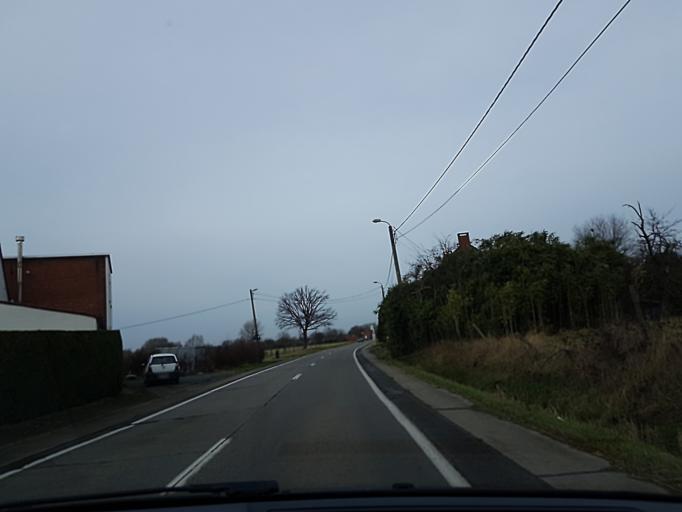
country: BE
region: Flanders
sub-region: Provincie Antwerpen
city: Putte
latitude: 51.0774
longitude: 4.6177
